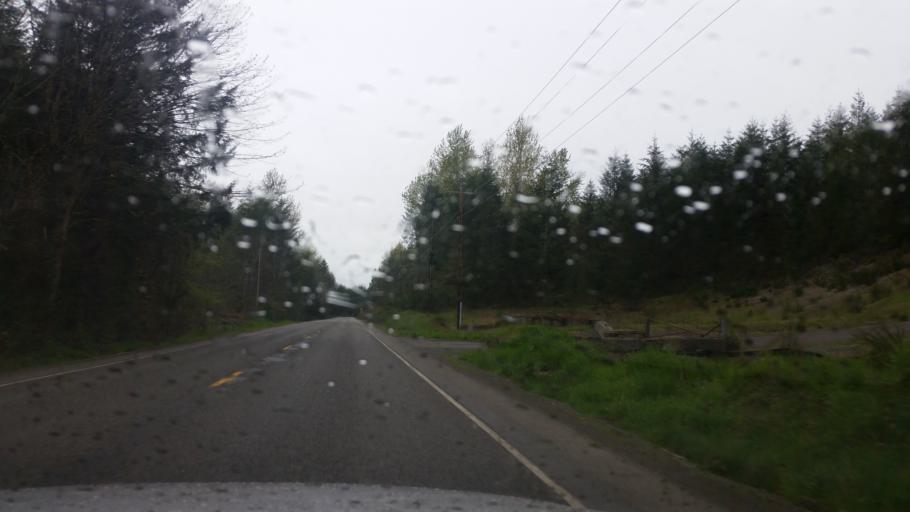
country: US
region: Washington
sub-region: Pierce County
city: Eatonville
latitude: 46.8643
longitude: -122.3198
